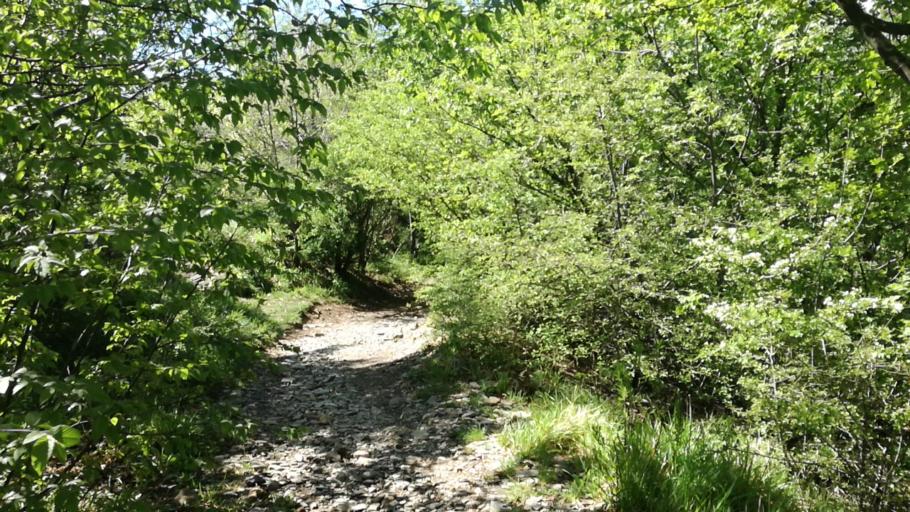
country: IT
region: Liguria
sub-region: Provincia di Genova
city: Manesseno
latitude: 44.4483
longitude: 8.9383
